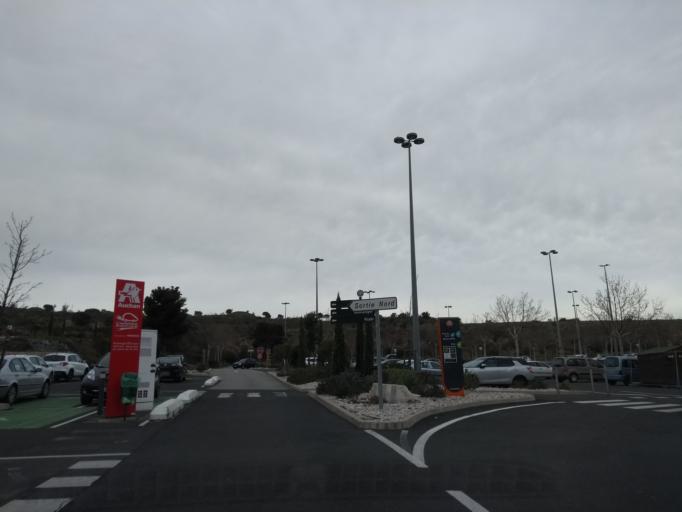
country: FR
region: Languedoc-Roussillon
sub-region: Departement des Pyrenees-Orientales
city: Pollestres
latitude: 42.6694
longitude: 2.8791
